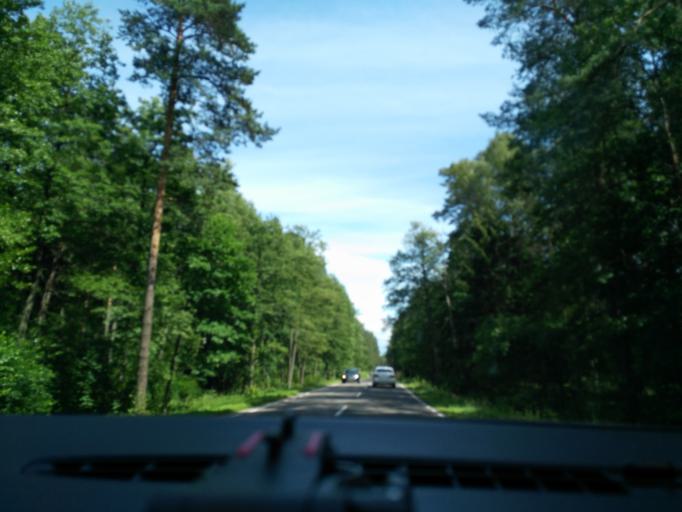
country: PL
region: Podlasie
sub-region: Powiat augustowski
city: Augustow
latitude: 53.8471
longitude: 23.0287
